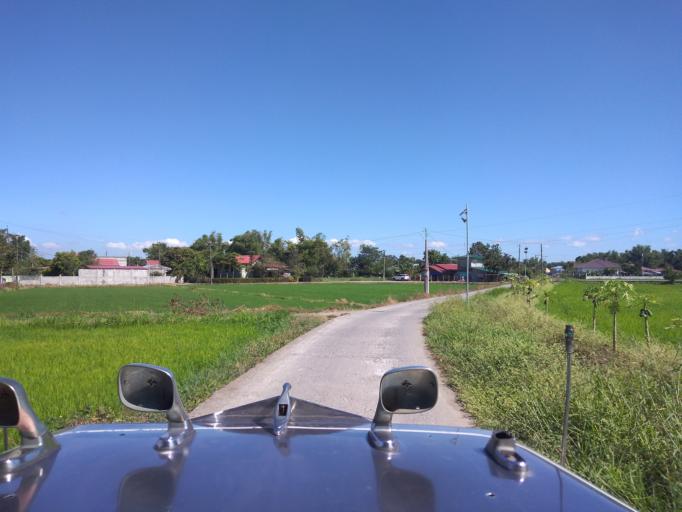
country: PH
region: Central Luzon
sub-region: Province of Pampanga
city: Salapungan
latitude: 15.1559
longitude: 120.9192
